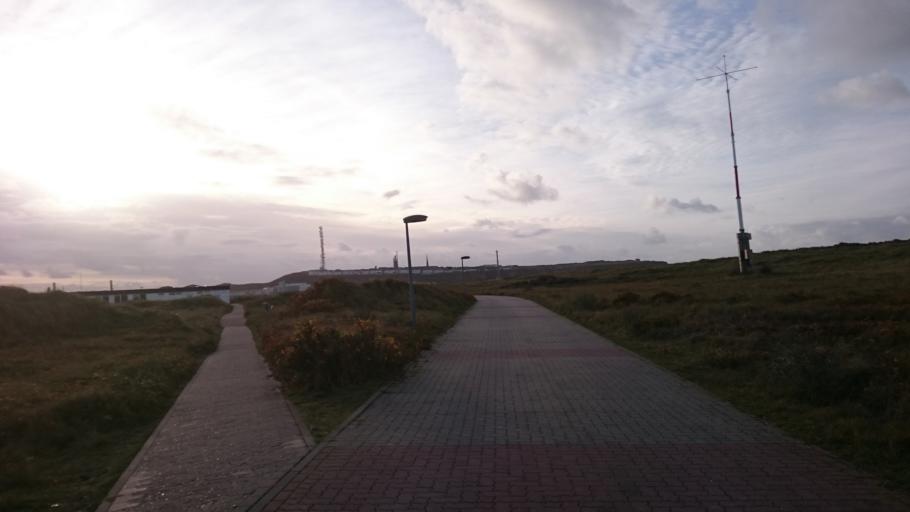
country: DE
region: Schleswig-Holstein
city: Helgoland
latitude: 54.1858
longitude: 7.9065
